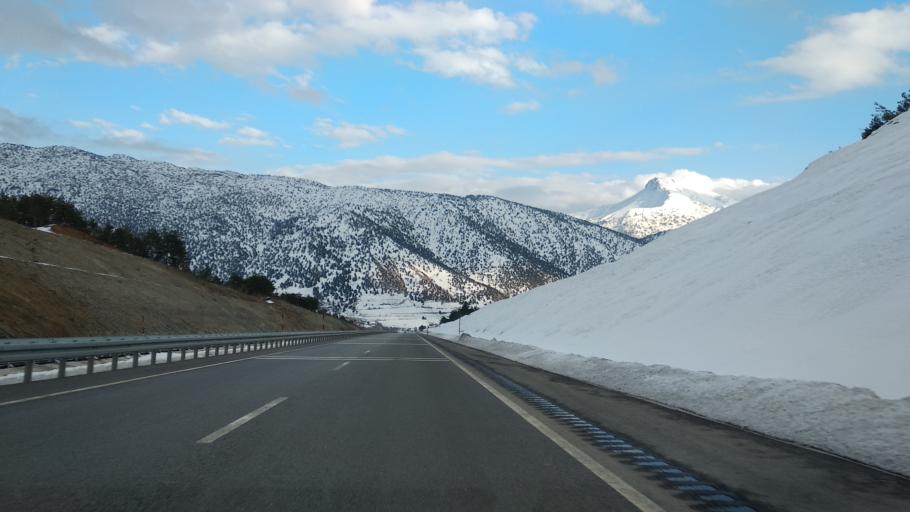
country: TR
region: Kahramanmaras
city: Goksun
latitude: 37.9052
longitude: 36.6001
